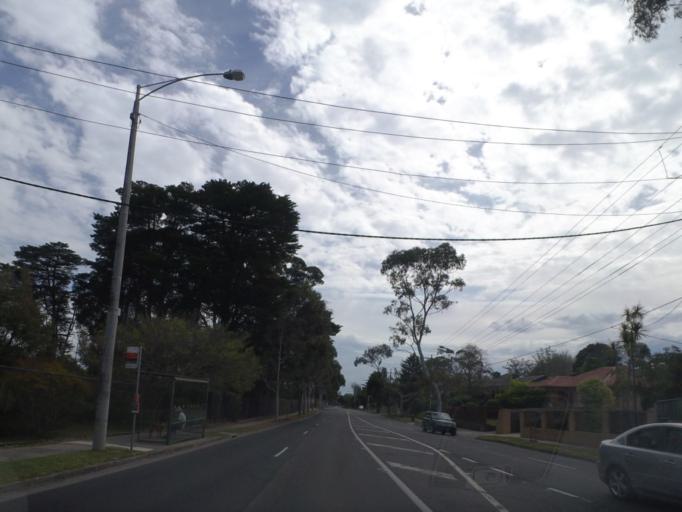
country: AU
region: Victoria
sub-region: Monash
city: Ashwood
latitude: -37.8688
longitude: 145.1181
